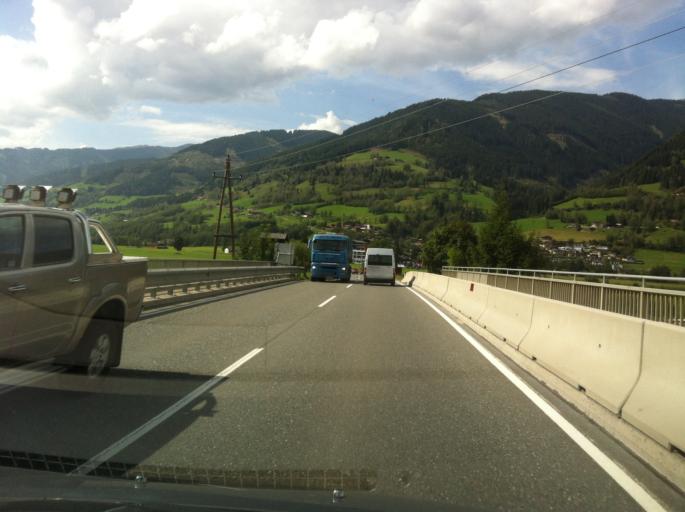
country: AT
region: Salzburg
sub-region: Politischer Bezirk Zell am See
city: Kaprun
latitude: 47.2843
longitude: 12.7519
